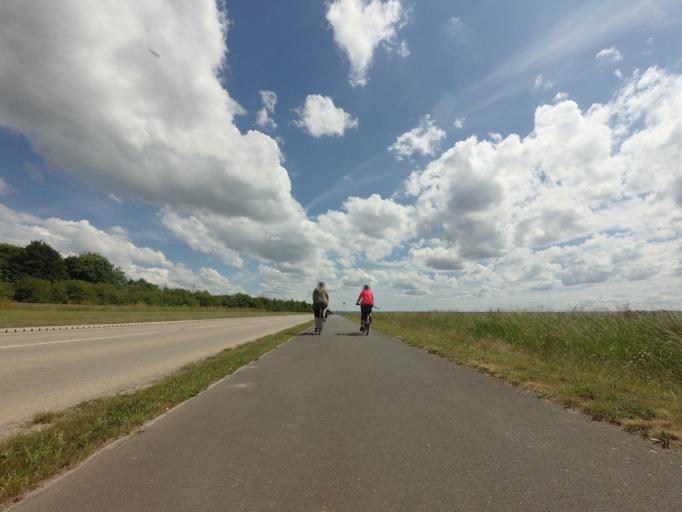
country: GB
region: England
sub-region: Kent
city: Hoo
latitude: 51.4314
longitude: 0.5726
